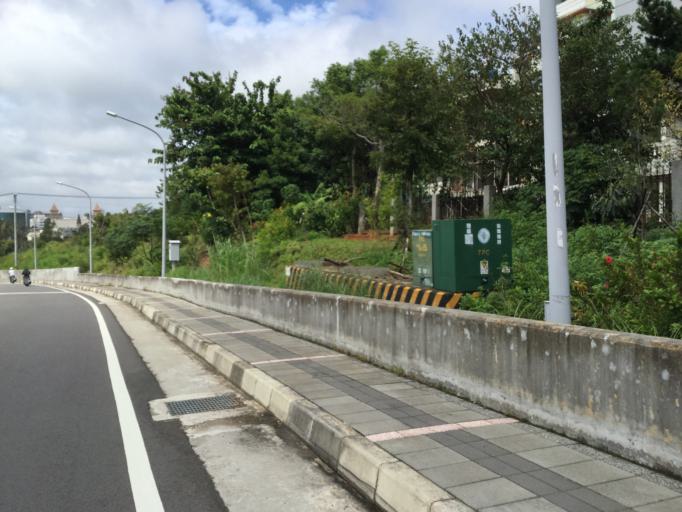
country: TW
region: Taiwan
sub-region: Hsinchu
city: Hsinchu
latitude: 24.7801
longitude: 121.0159
